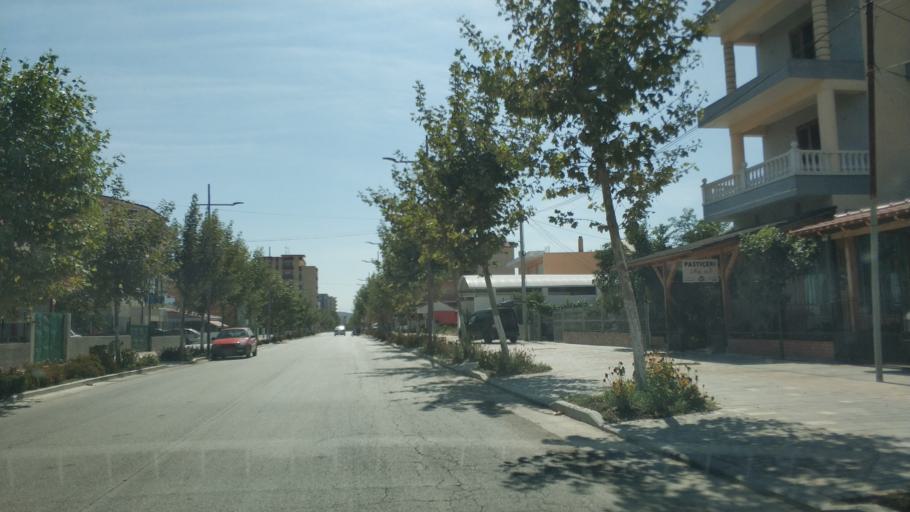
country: AL
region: Fier
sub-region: Rrethi i Lushnjes
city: Divjake
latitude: 41.0009
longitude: 19.5308
